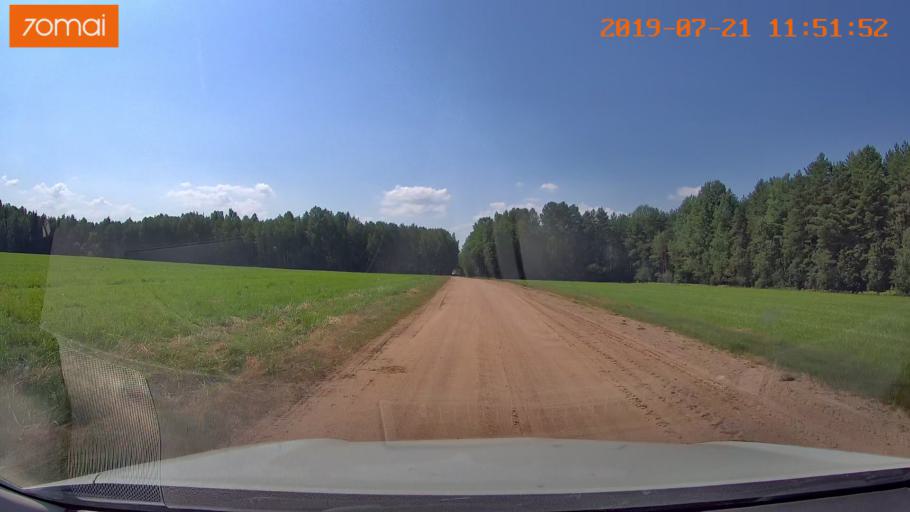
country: BY
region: Grodnenskaya
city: Lyubcha
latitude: 53.8812
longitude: 26.0106
